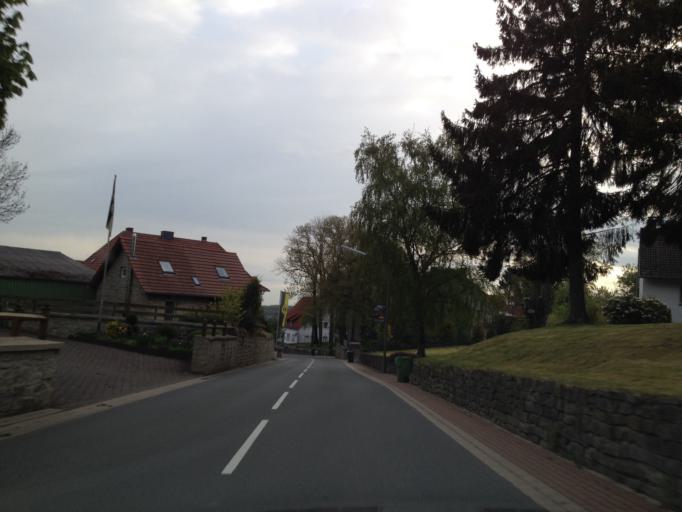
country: DE
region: North Rhine-Westphalia
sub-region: Regierungsbezirk Arnsberg
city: Anrochte
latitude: 51.5092
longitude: 8.2882
